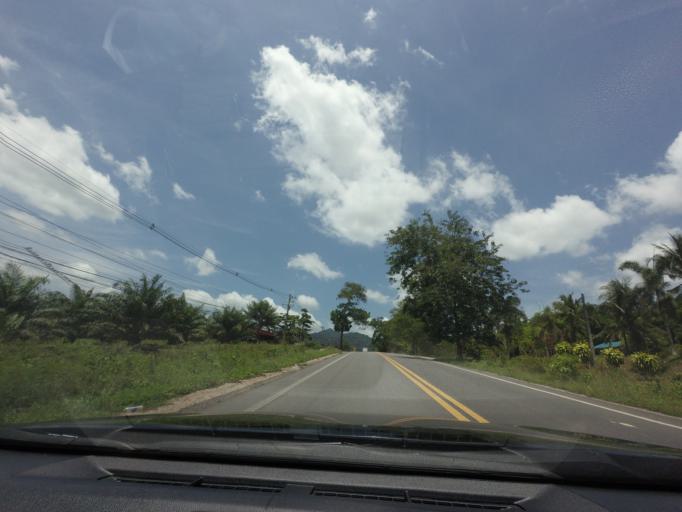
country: TH
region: Chumphon
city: Ban Nam Yuen
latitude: 9.9058
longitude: 98.9005
